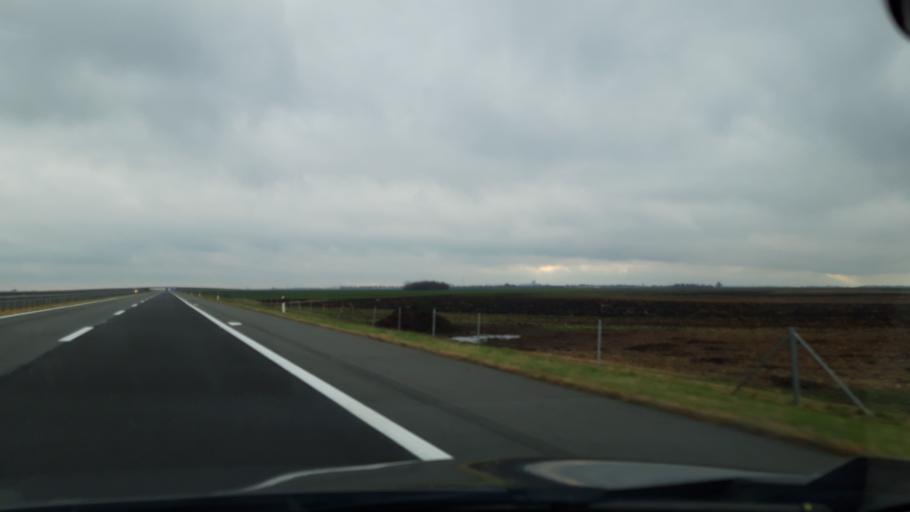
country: RS
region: Autonomna Pokrajina Vojvodina
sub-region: Severnobacki Okrug
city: Backa Topola
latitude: 45.8506
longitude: 19.6954
